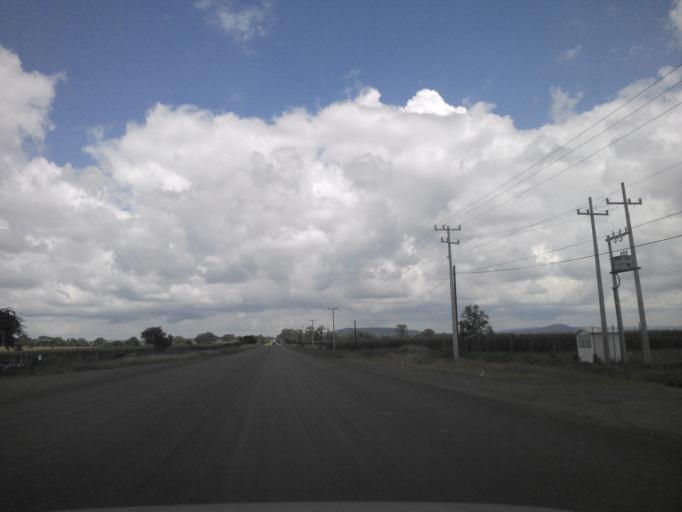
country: MX
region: Jalisco
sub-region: Atotonilco el Alto
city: Ojo de Agua de Moran
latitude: 20.5929
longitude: -102.4949
